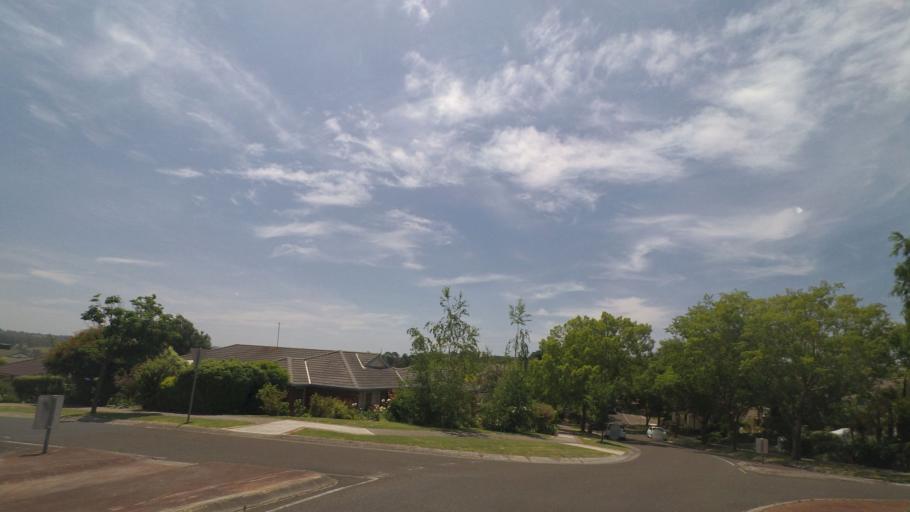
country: AU
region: Victoria
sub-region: Yarra Ranges
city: Chirnside Park
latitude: -37.7588
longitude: 145.3052
